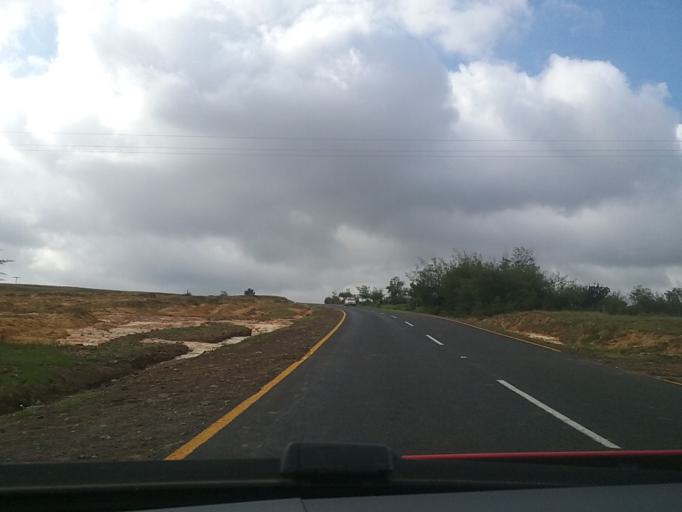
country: LS
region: Berea
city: Teyateyaneng
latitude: -29.1927
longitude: 27.8071
